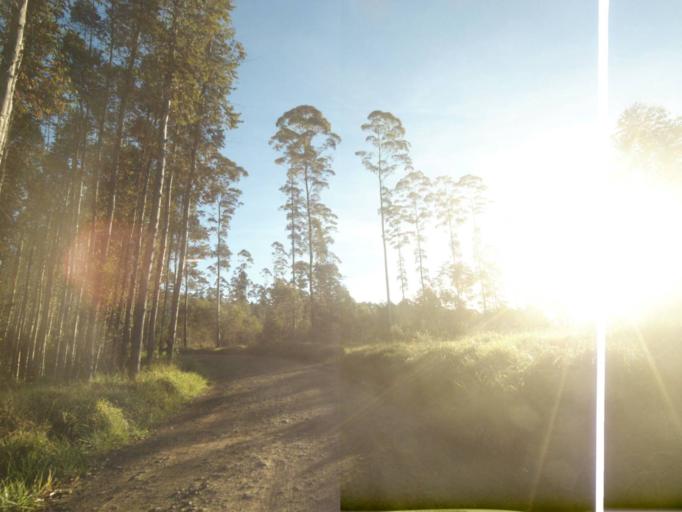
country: BR
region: Parana
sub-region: Telemaco Borba
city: Telemaco Borba
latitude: -24.4917
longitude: -50.5959
